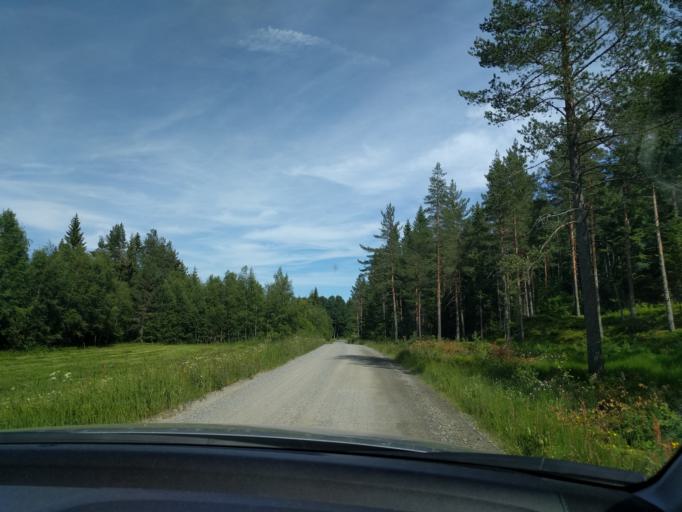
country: NO
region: Aust-Agder
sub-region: Gjerstad
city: Gjerstad
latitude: 58.8813
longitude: 8.9331
